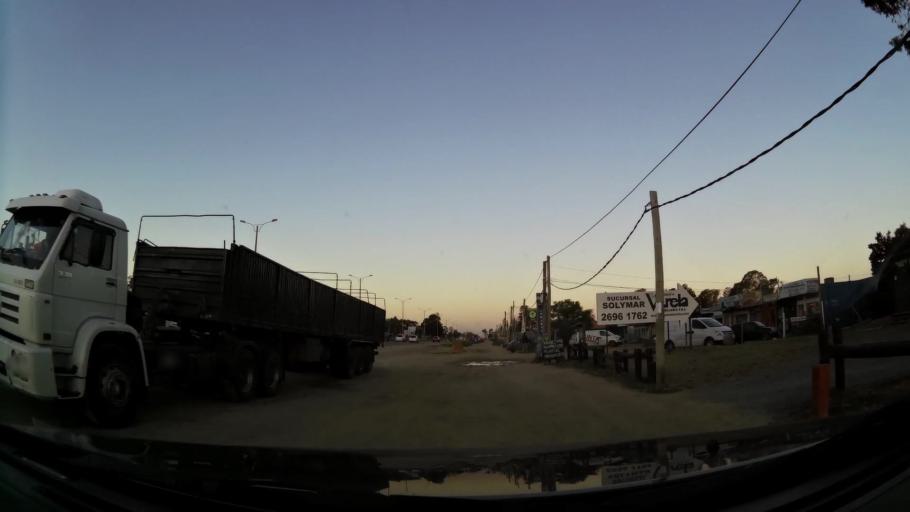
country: UY
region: Canelones
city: Colonia Nicolich
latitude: -34.8256
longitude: -55.9646
